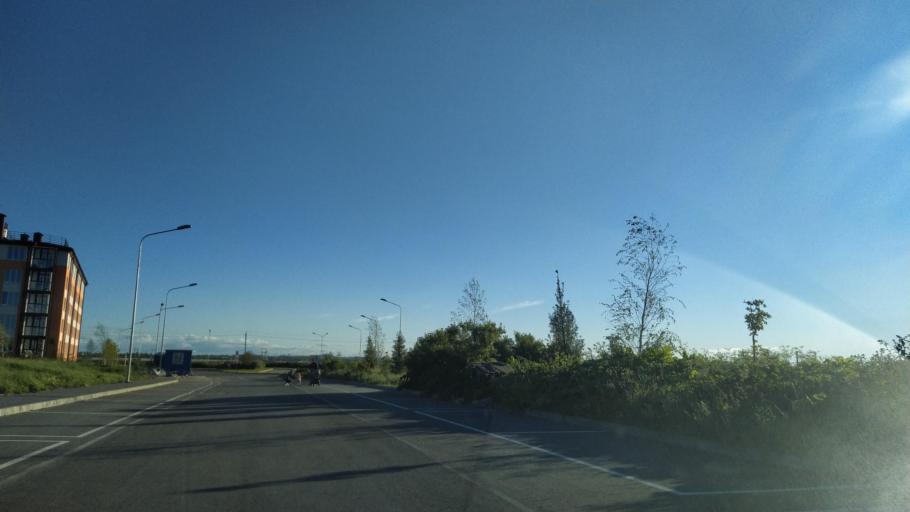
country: RU
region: St.-Petersburg
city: Aleksandrovskaya
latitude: 59.7554
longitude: 30.3598
